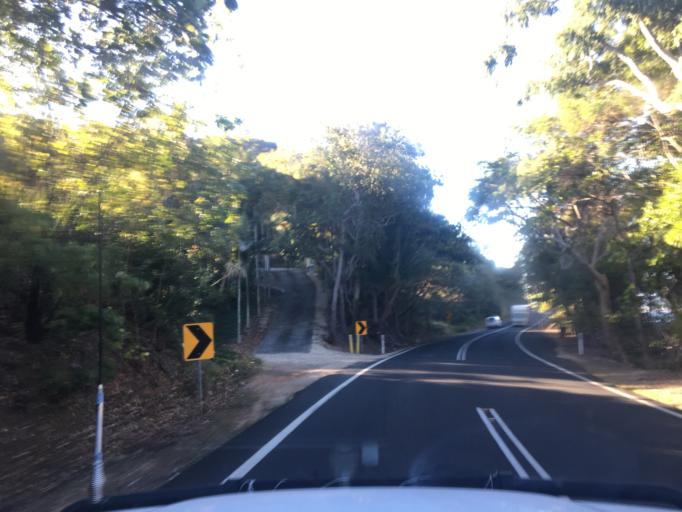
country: AU
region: Queensland
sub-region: Cairns
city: Port Douglas
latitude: -16.5778
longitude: 145.5118
